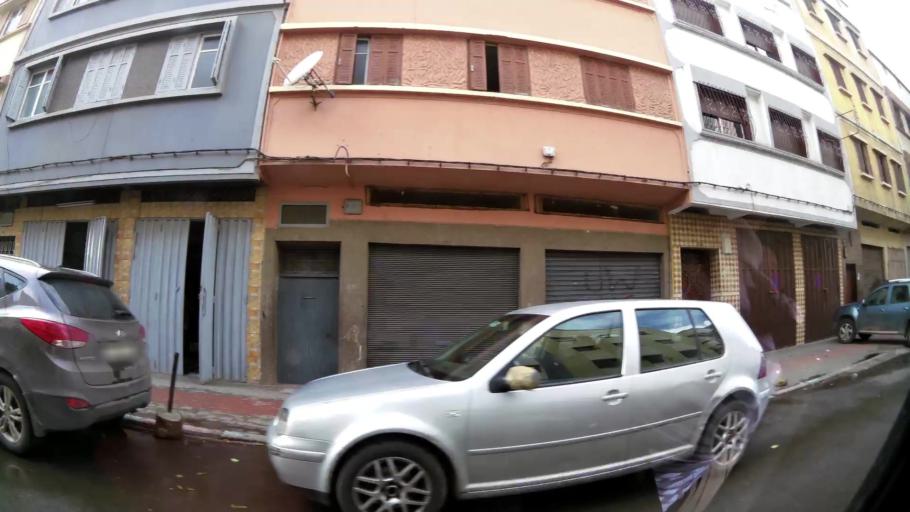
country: MA
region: Grand Casablanca
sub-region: Casablanca
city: Casablanca
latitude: 33.5456
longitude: -7.5755
